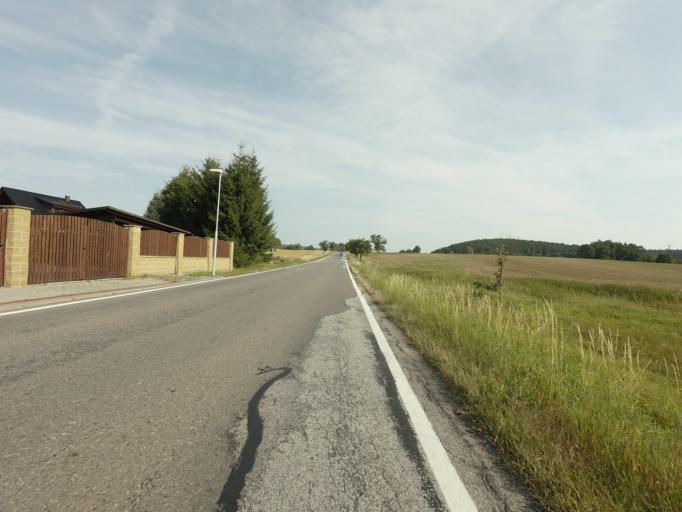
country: CZ
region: Jihocesky
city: Milevsko
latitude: 49.4633
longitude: 14.3626
